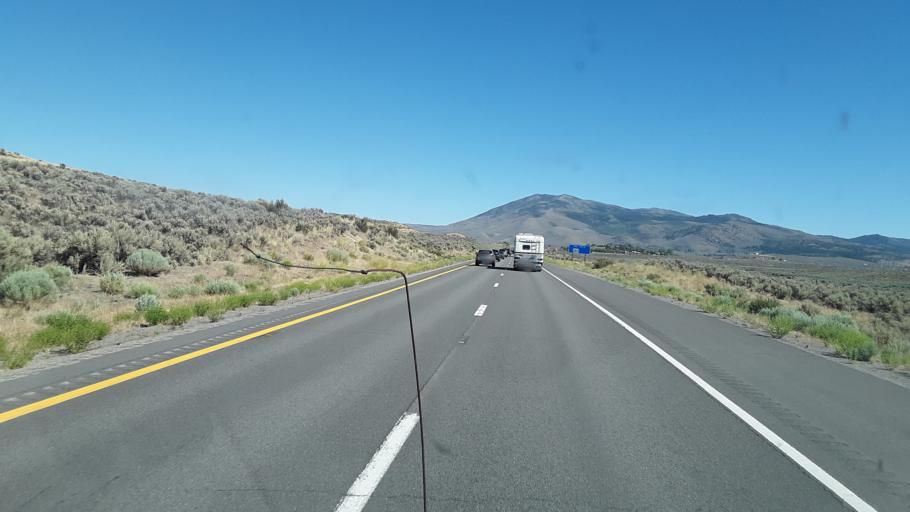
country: US
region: Nevada
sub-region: Washoe County
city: Cold Springs
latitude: 39.6823
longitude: -120.0105
